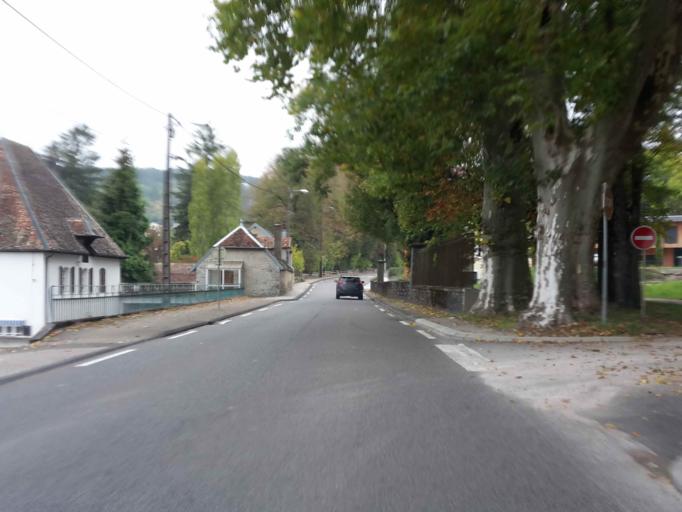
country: FR
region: Franche-Comte
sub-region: Departement du Doubs
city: Baume-les-Dames
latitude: 47.3470
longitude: 6.3610
